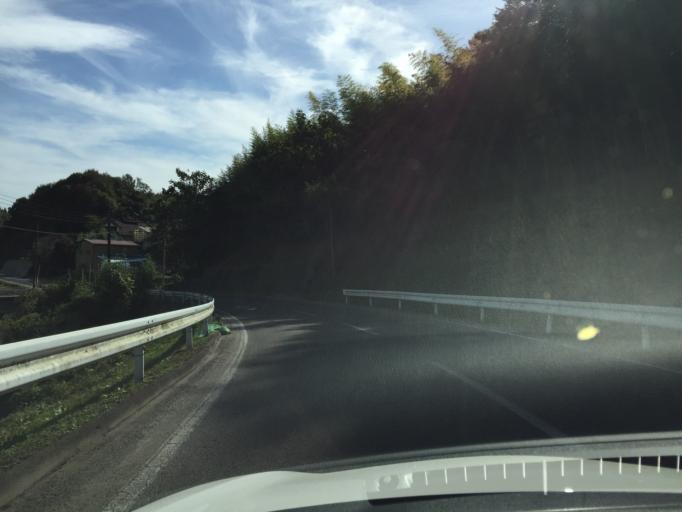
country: JP
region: Fukushima
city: Miharu
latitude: 37.4601
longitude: 140.4921
